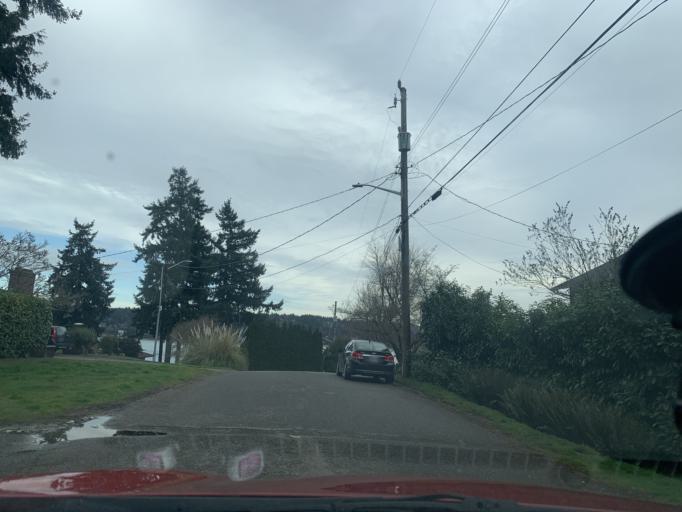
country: US
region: Washington
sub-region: King County
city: Bryn Mawr-Skyway
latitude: 47.5317
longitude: -122.2649
